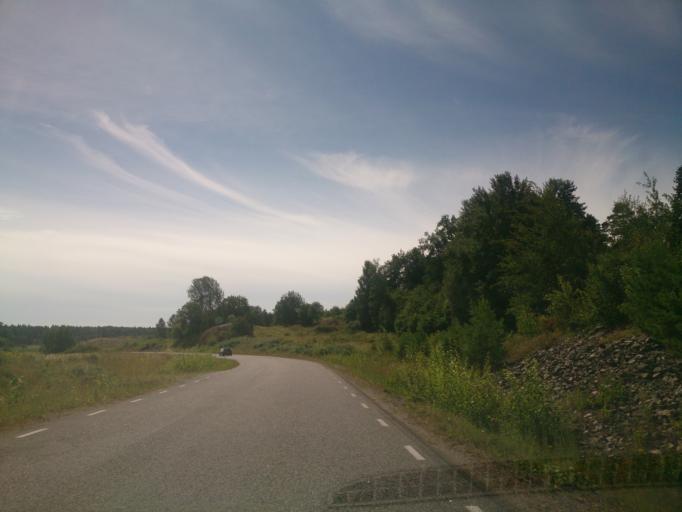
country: SE
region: OEstergoetland
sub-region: Valdemarsviks Kommun
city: Valdemarsvik
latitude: 58.2910
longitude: 16.6692
